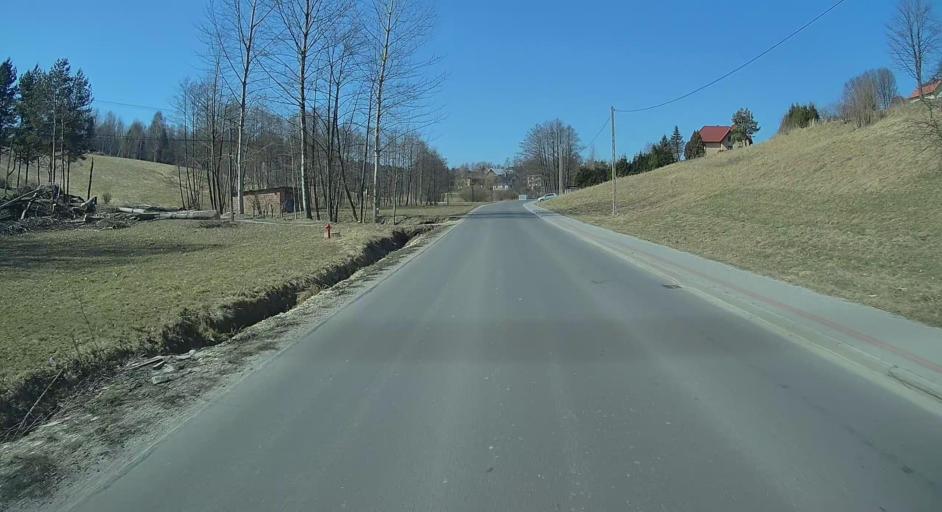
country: PL
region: Subcarpathian Voivodeship
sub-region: Powiat przeworski
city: Jawornik Polski
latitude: 49.8871
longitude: 22.2311
